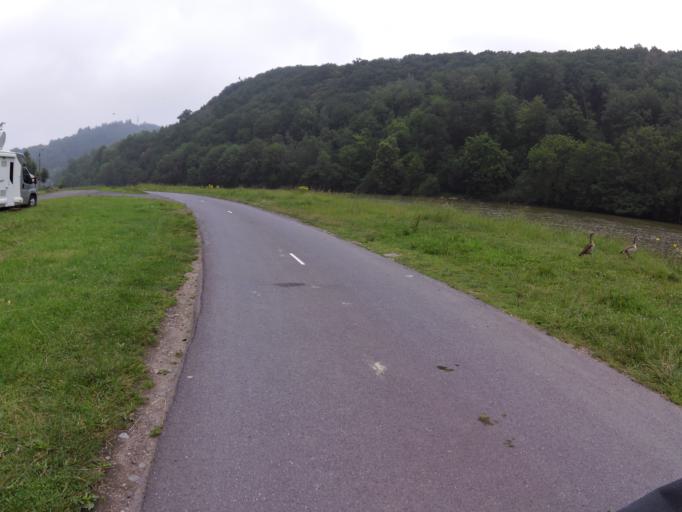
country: FR
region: Champagne-Ardenne
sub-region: Departement des Ardennes
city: Fumay
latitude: 49.9973
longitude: 4.7095
